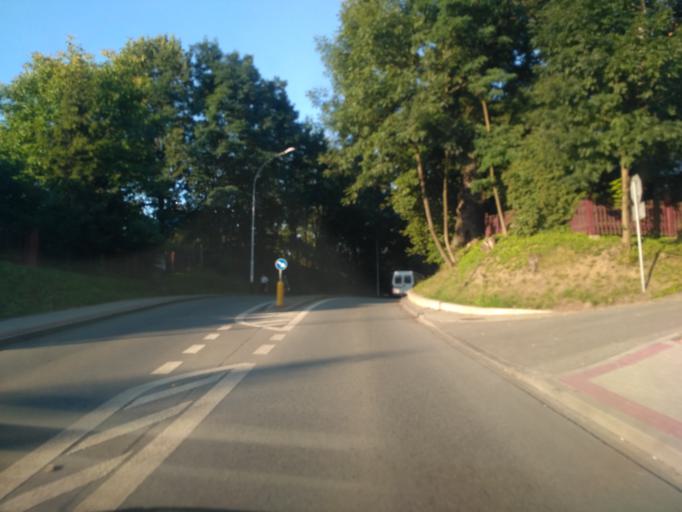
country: PL
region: Subcarpathian Voivodeship
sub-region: Krosno
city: Krosno
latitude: 49.6963
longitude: 21.7794
